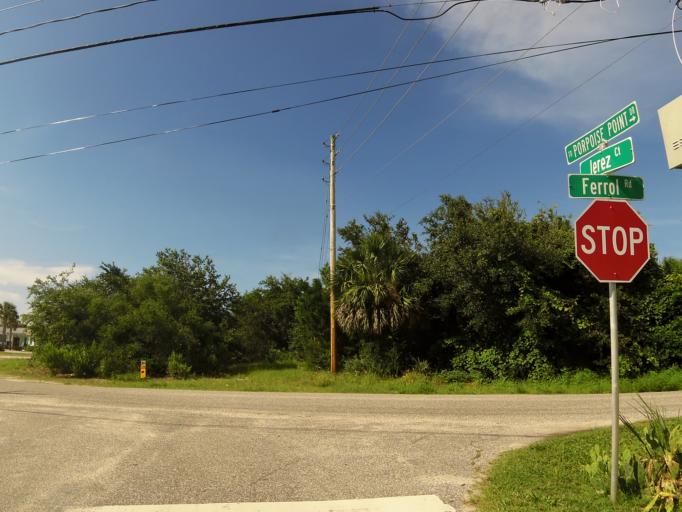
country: US
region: Florida
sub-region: Saint Johns County
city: Villano Beach
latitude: 29.9160
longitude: -81.2963
